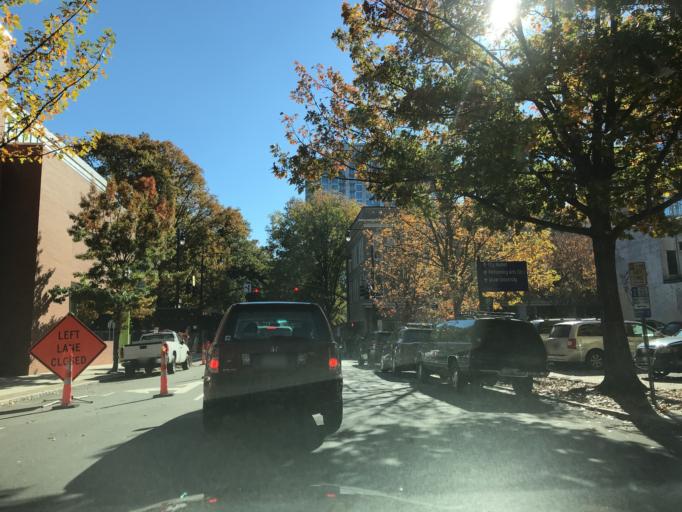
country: US
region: North Carolina
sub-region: Wake County
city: Raleigh
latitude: 35.7787
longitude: -78.6366
